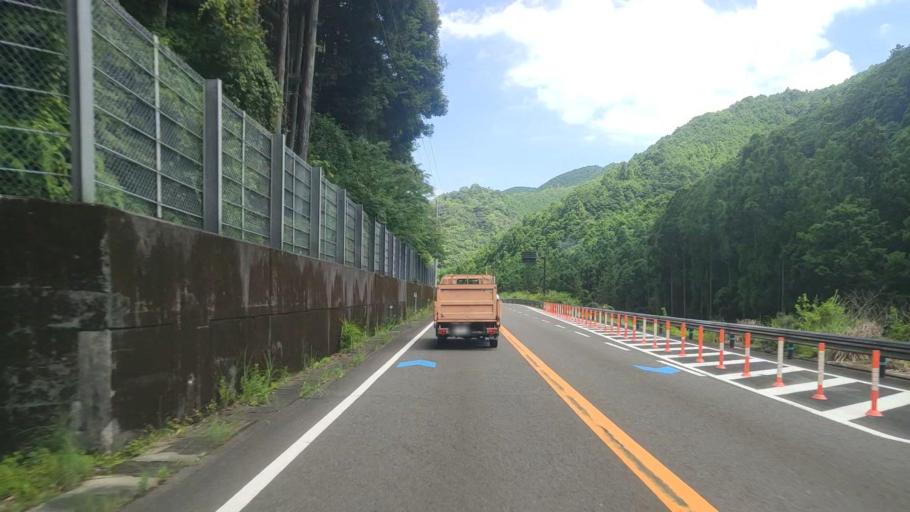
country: JP
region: Mie
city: Owase
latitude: 33.9250
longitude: 136.0929
